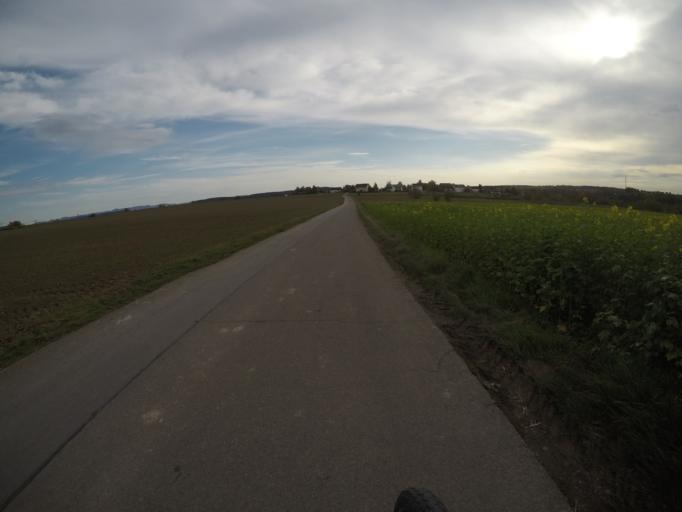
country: DE
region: Baden-Wuerttemberg
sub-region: Regierungsbezirk Stuttgart
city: Herrenberg
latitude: 48.5492
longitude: 8.9224
